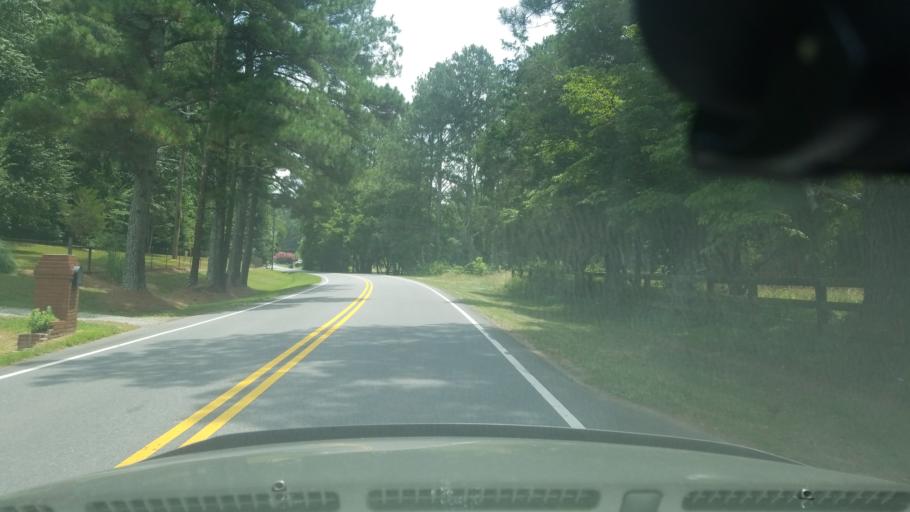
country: US
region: Georgia
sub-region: Fulton County
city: Milton
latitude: 34.1584
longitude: -84.2654
